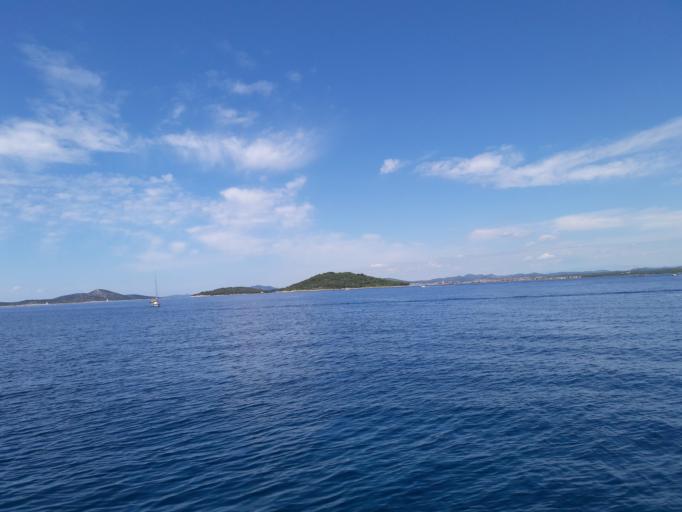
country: HR
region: Sibensko-Kniniska
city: Vodice
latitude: 43.7033
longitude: 15.8298
